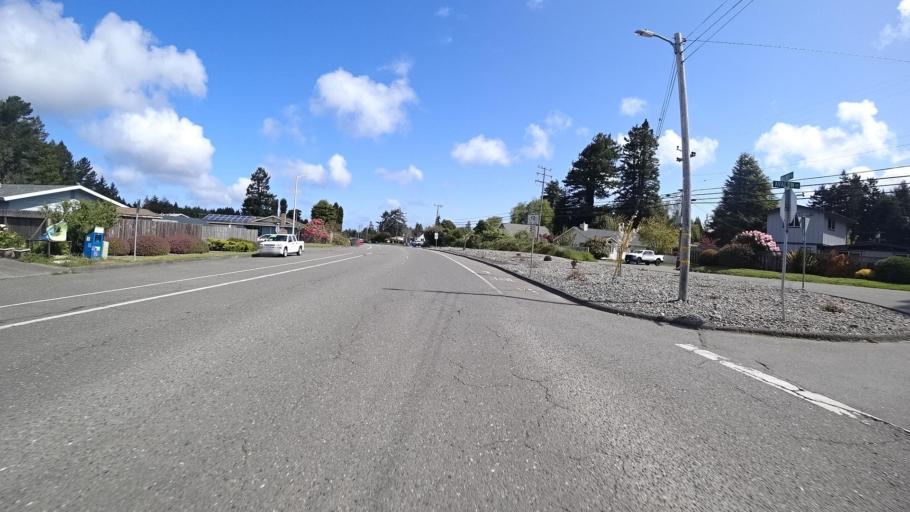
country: US
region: California
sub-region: Humboldt County
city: Pine Hills
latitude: 40.7370
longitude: -124.1478
